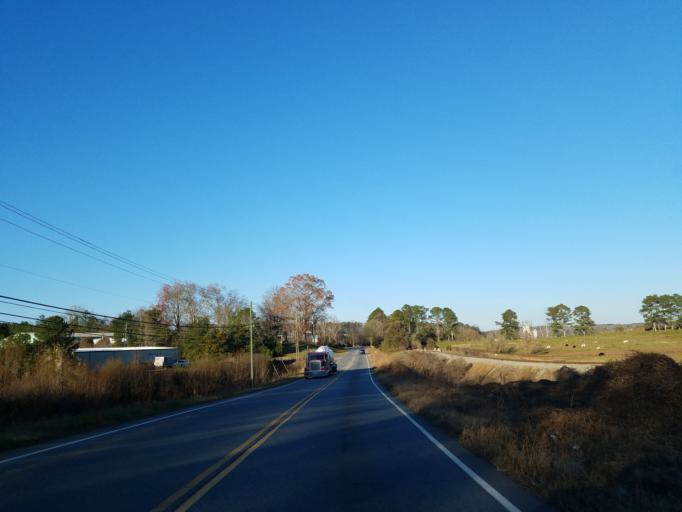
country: US
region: Georgia
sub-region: Cherokee County
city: Ball Ground
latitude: 34.2978
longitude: -84.4163
